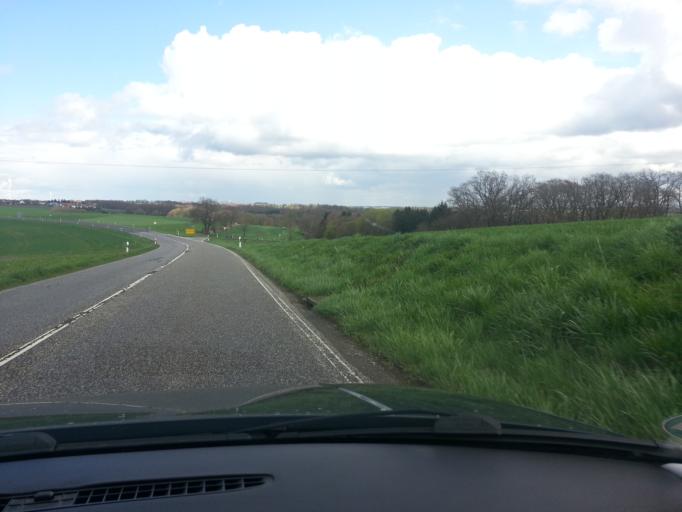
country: DE
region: Rheinland-Pfalz
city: Kashofen
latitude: 49.3324
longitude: 7.4244
